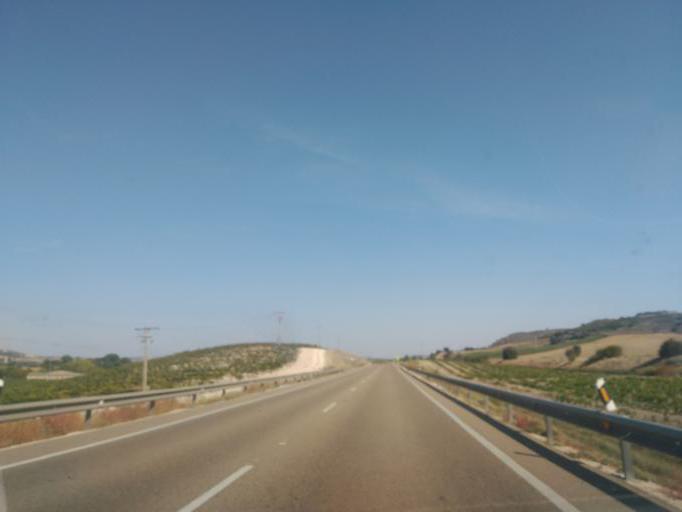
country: ES
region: Castille and Leon
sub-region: Provincia de Valladolid
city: Valbuena de Duero
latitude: 41.6239
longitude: -4.2647
